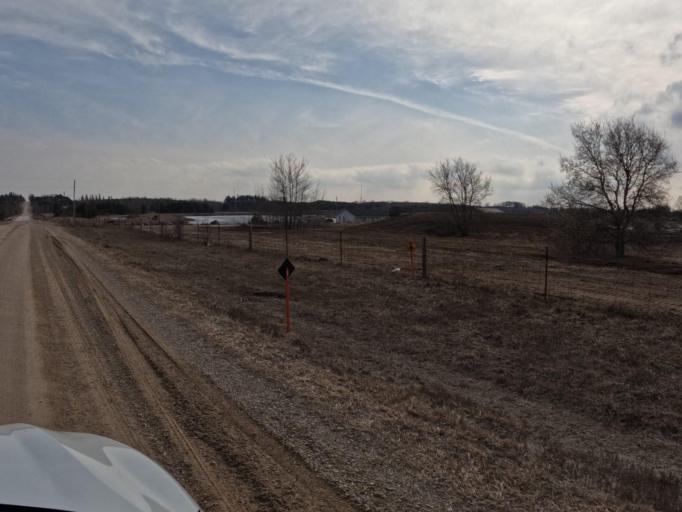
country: CA
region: Ontario
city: Orangeville
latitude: 43.8960
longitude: -80.3004
